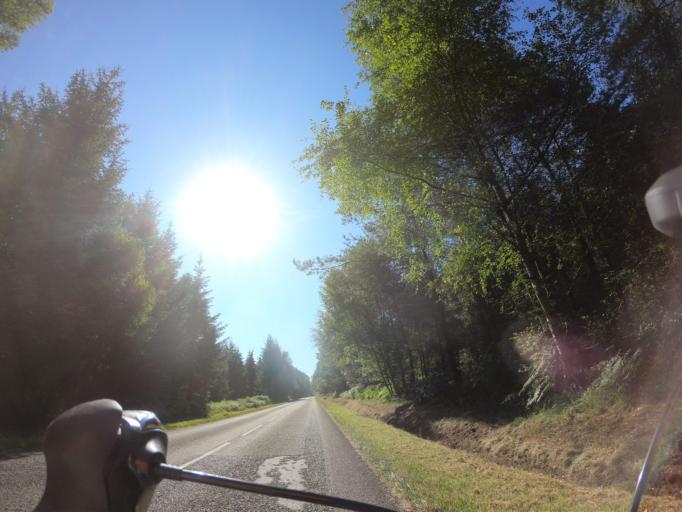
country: FR
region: Lower Normandy
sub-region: Departement de l'Orne
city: Juvigny-sous-Andaine
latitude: 48.5813
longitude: -0.4742
